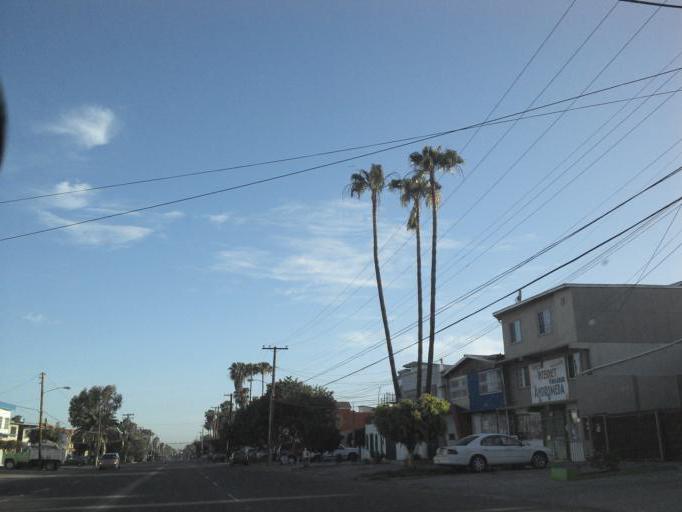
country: MX
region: Baja California
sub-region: Tijuana
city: La Esperanza [Granjas Familiares]
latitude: 32.5144
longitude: -117.1162
